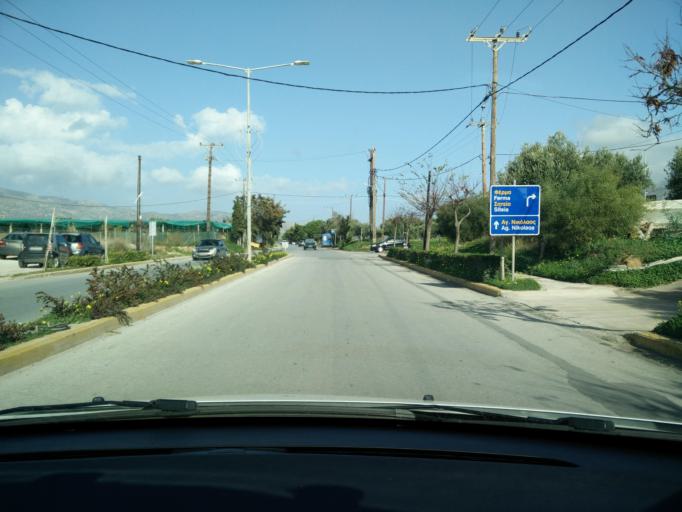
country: GR
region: Crete
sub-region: Nomos Lasithiou
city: Ierapetra
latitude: 35.0174
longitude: 25.7472
